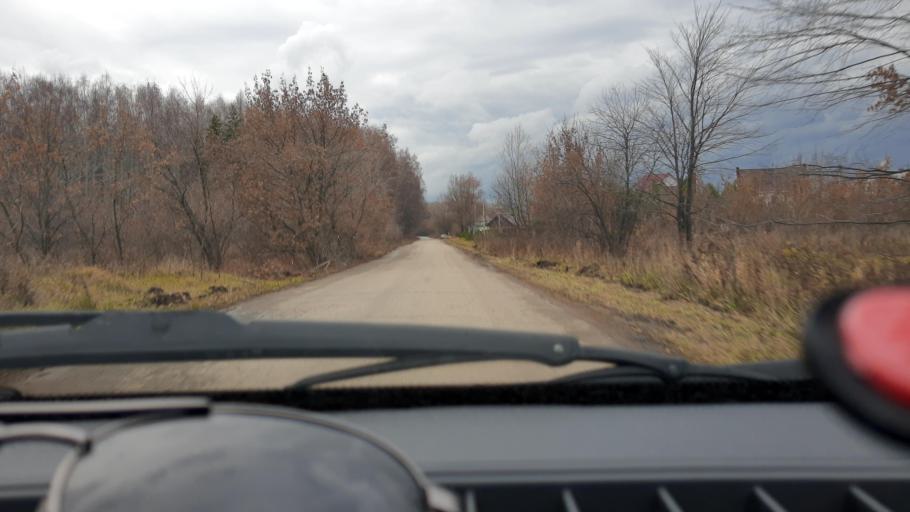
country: RU
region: Bashkortostan
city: Ufa
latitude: 54.7874
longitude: 56.1599
